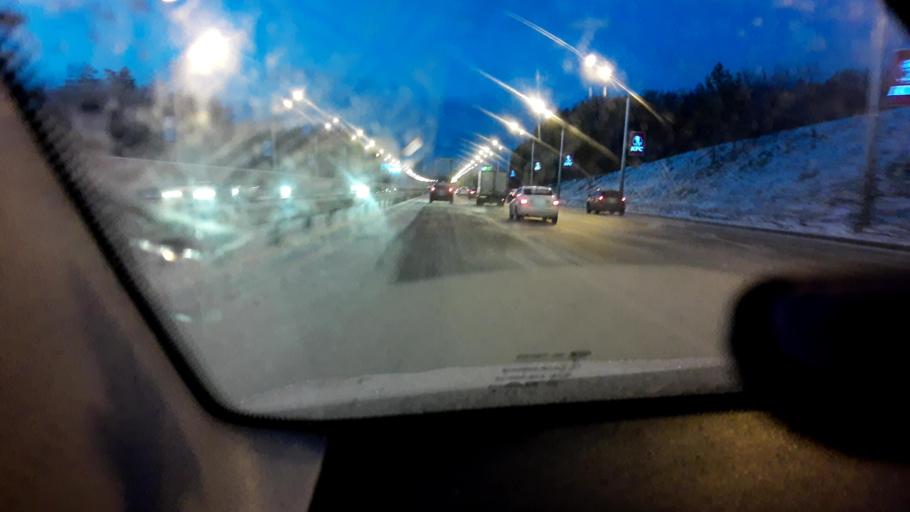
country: RU
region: Bashkortostan
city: Ufa
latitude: 54.7461
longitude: 56.0125
